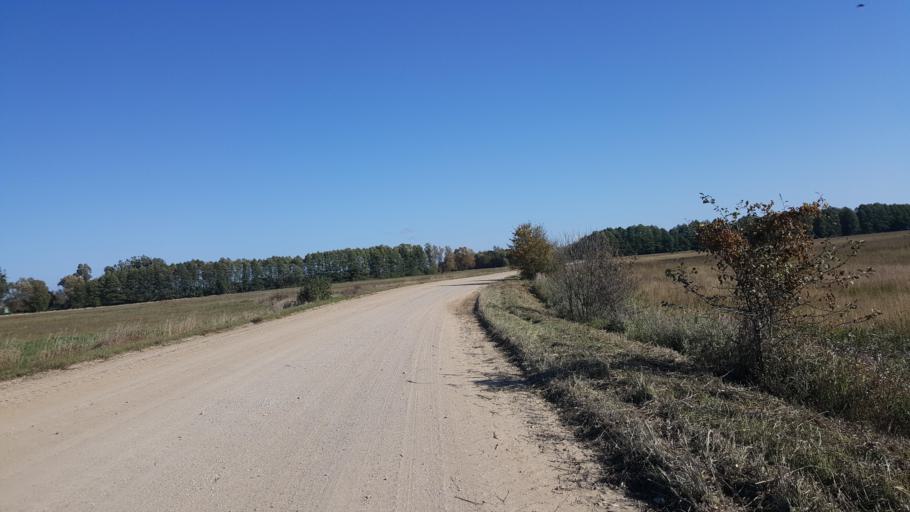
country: BY
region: Brest
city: Kamyanyets
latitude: 52.4205
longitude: 23.8714
